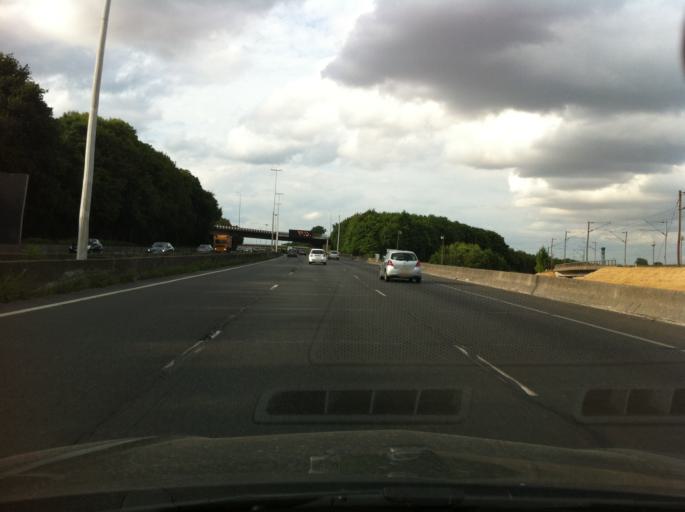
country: FR
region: Ile-de-France
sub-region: Departement du Val-d'Oise
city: Roissy-en-France
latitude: 49.0034
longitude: 2.5248
